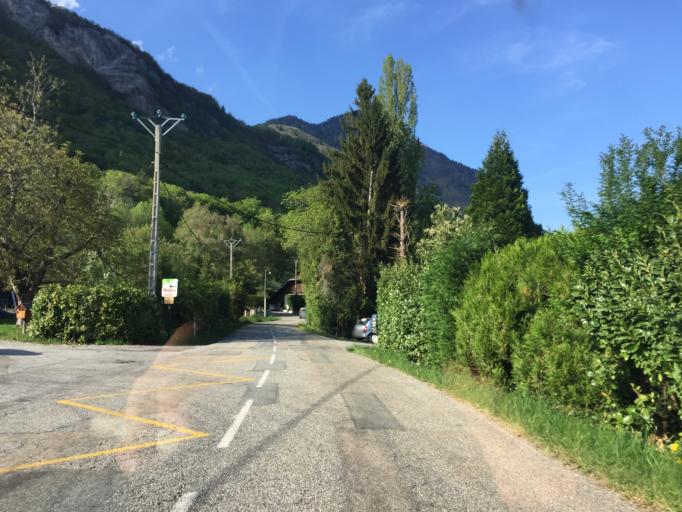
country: FR
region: Rhone-Alpes
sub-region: Departement de la Savoie
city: Mercury
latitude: 45.6660
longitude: 6.3195
